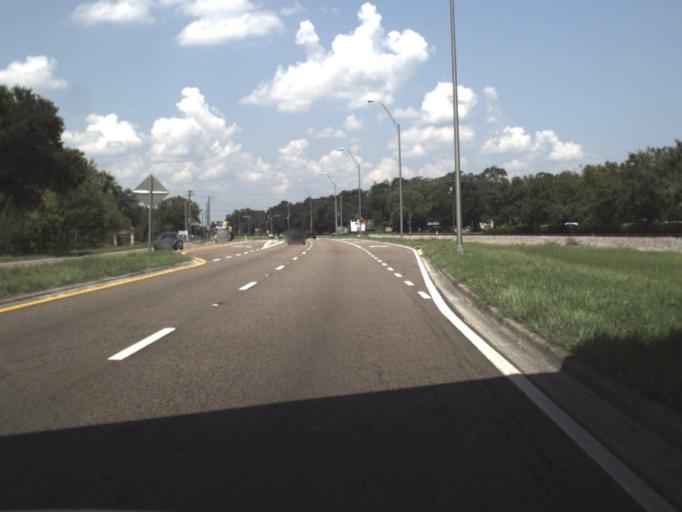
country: US
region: Florida
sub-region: Hillsborough County
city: Lake Magdalene
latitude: 28.0967
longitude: -82.4520
